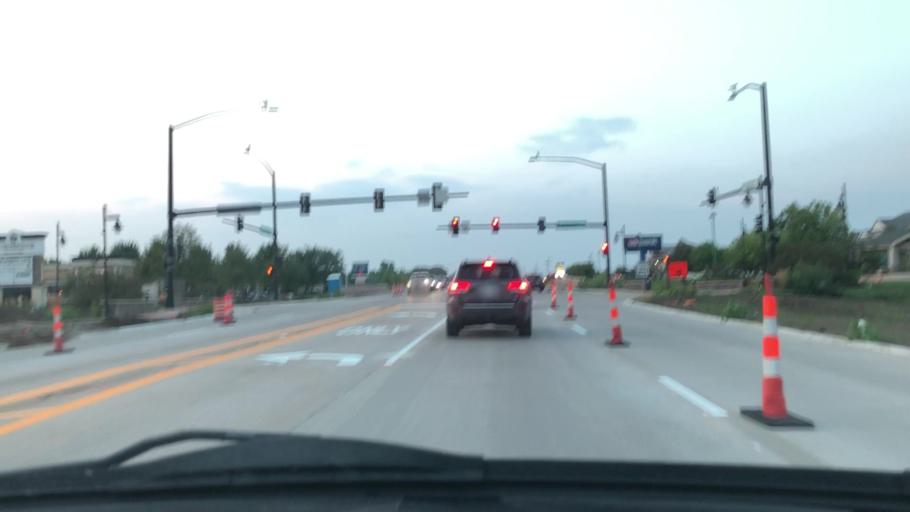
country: US
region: Iowa
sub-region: Johnson County
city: North Liberty
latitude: 41.7489
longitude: -91.6076
